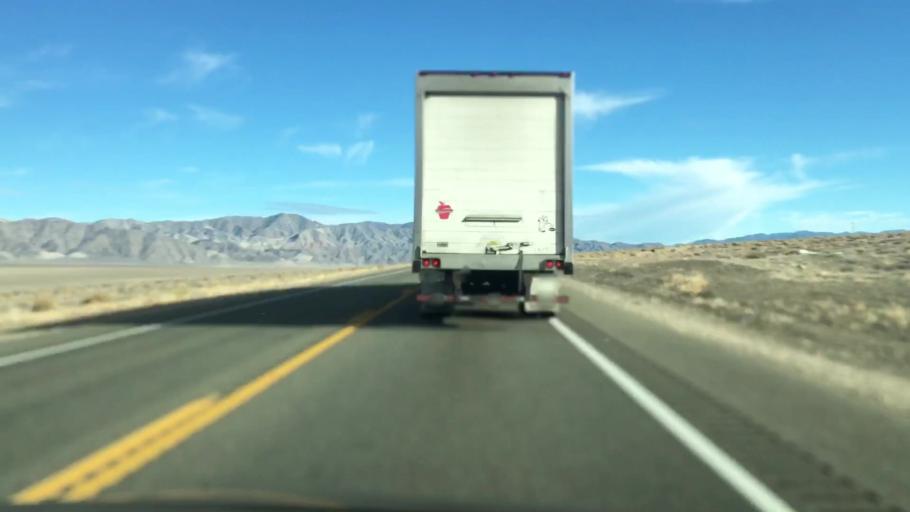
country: US
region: Nevada
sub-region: Mineral County
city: Hawthorne
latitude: 38.5317
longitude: -118.2791
